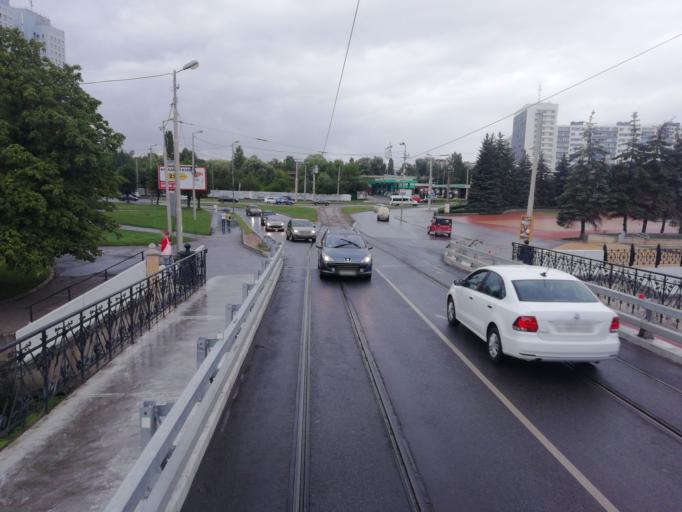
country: RU
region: Kaliningrad
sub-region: Gorod Kaliningrad
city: Kaliningrad
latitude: 54.7074
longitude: 20.5144
